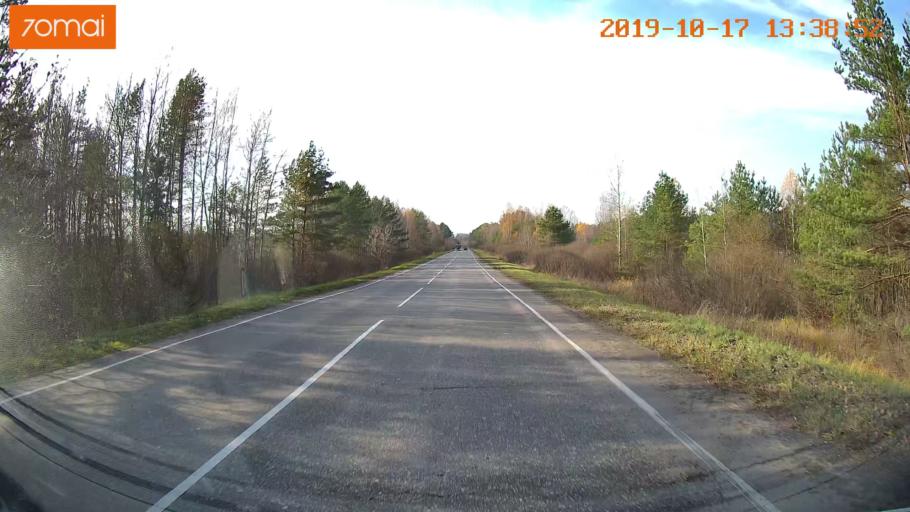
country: RU
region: Rjazan
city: Tuma
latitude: 55.1449
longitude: 40.6025
